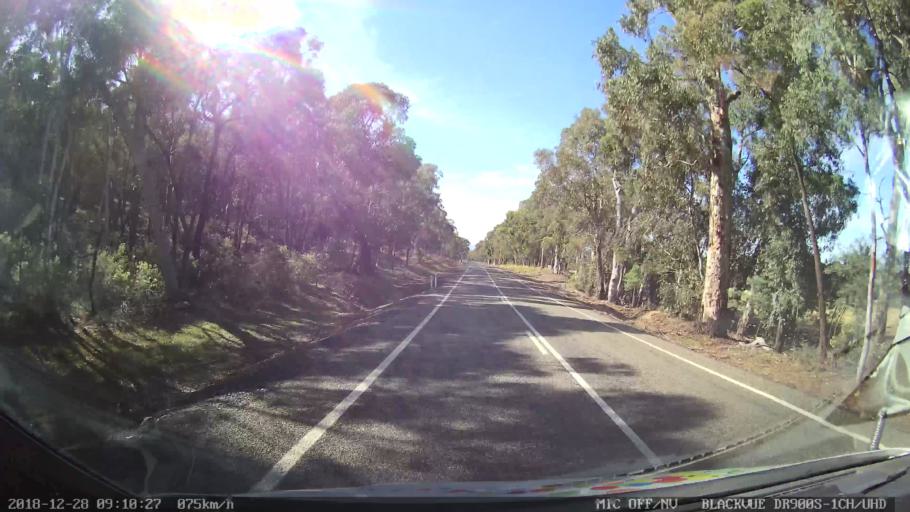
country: AU
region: New South Wales
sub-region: Upper Lachlan Shire
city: Crookwell
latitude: -34.2320
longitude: 149.3365
